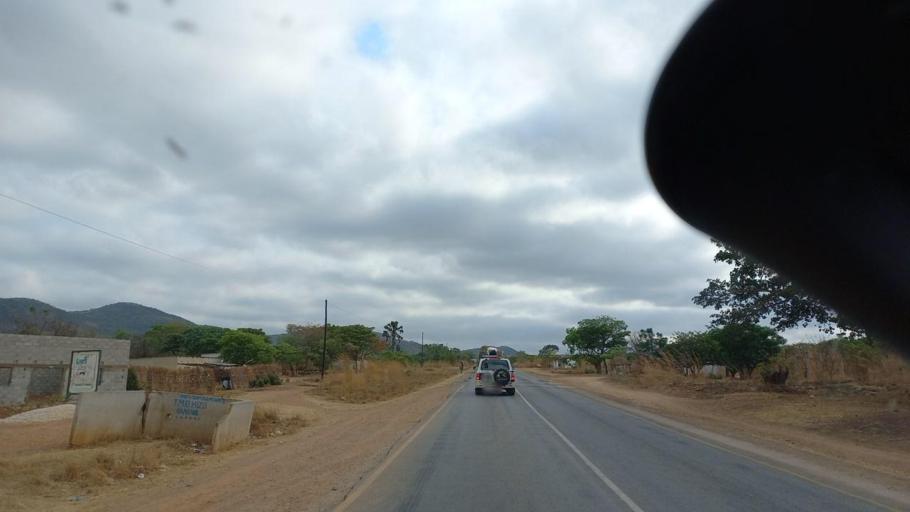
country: ZM
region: Lusaka
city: Chongwe
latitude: -15.2410
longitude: 29.1635
